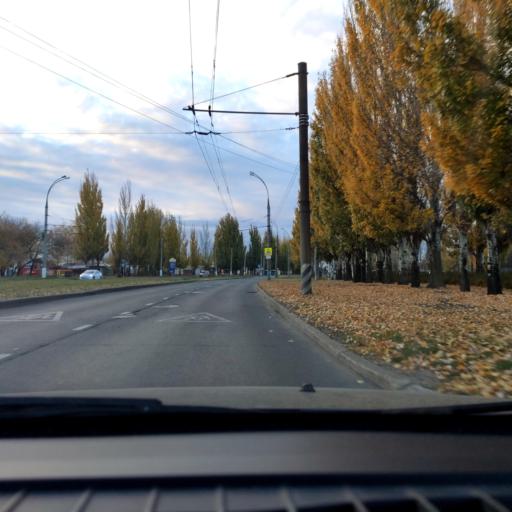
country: RU
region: Samara
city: Tol'yatti
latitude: 53.5435
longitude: 49.2785
